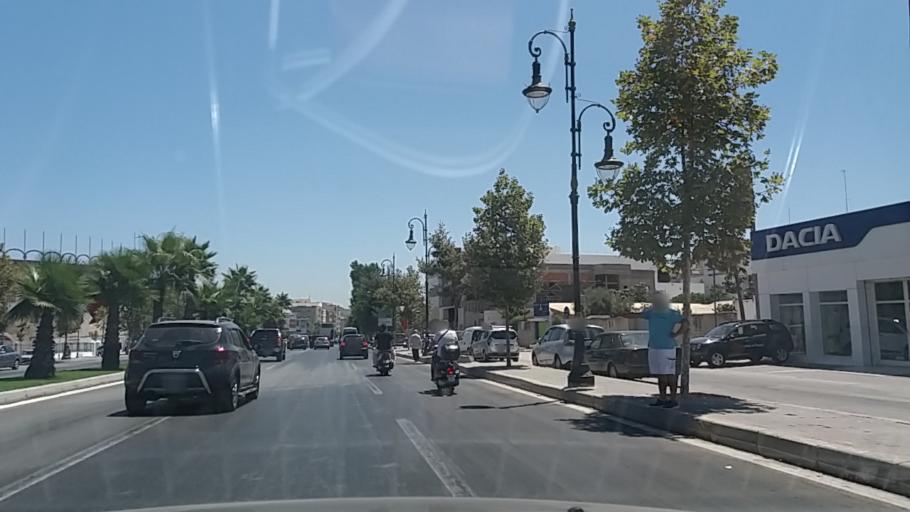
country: MA
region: Tanger-Tetouan
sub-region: Tanger-Assilah
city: Tangier
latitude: 35.7652
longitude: -5.7983
